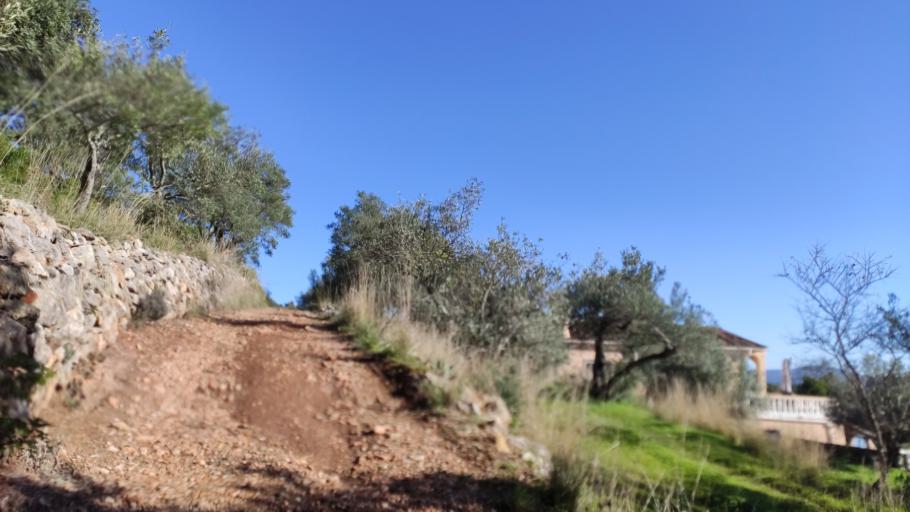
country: PT
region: Faro
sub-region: Sao Bras de Alportel
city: Sao Bras de Alportel
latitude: 37.1561
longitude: -7.9100
